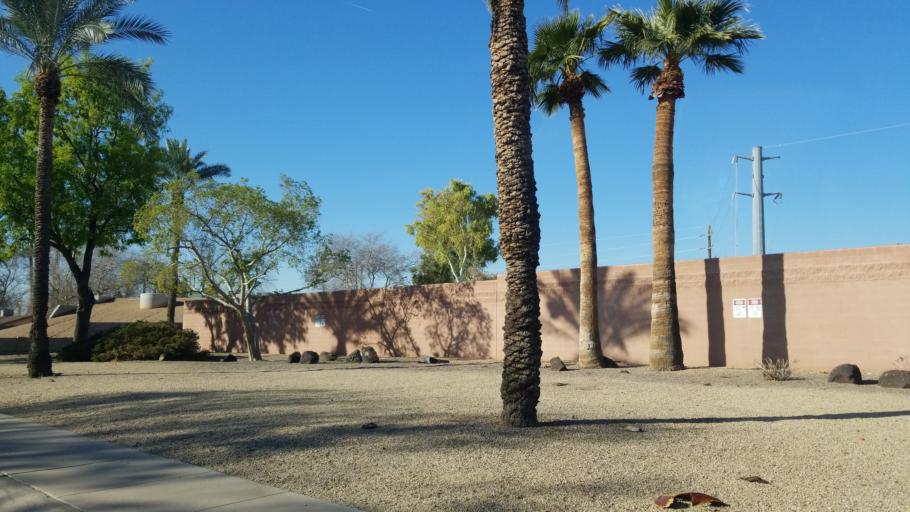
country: US
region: Arizona
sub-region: Maricopa County
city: Phoenix
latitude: 33.5304
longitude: -112.0945
